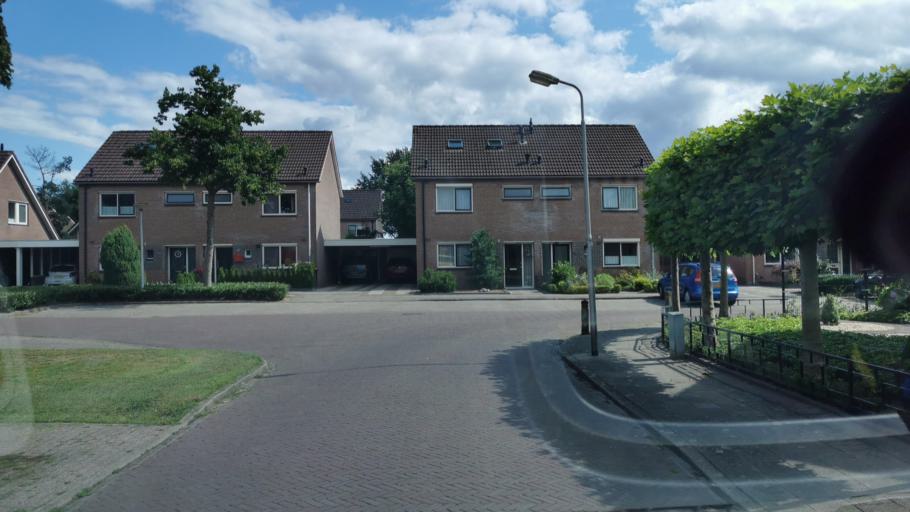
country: DE
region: North Rhine-Westphalia
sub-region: Regierungsbezirk Munster
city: Gronau
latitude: 52.2372
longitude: 7.0445
